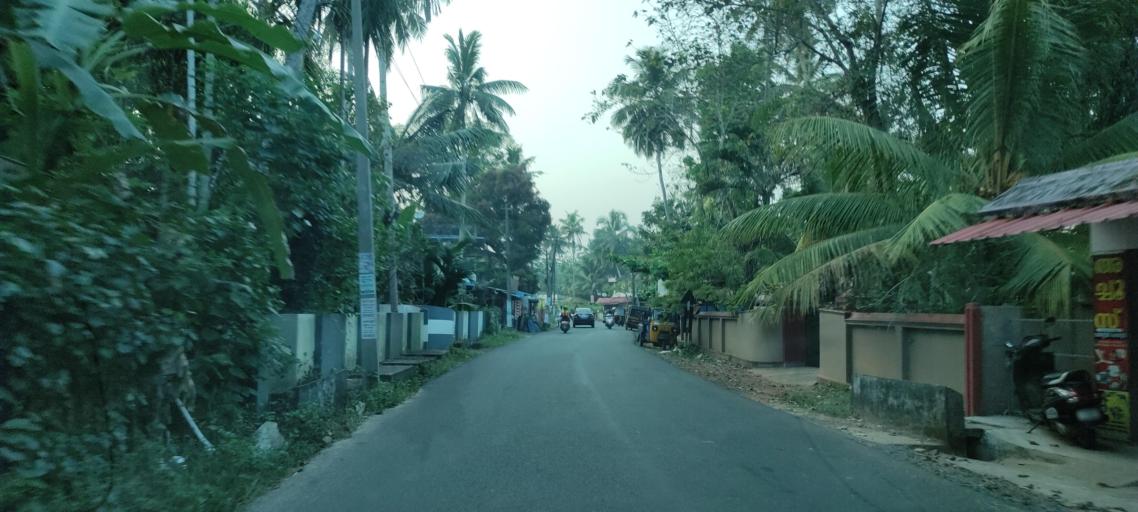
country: IN
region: Kerala
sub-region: Alappuzha
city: Kayankulam
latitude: 9.1364
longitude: 76.5234
